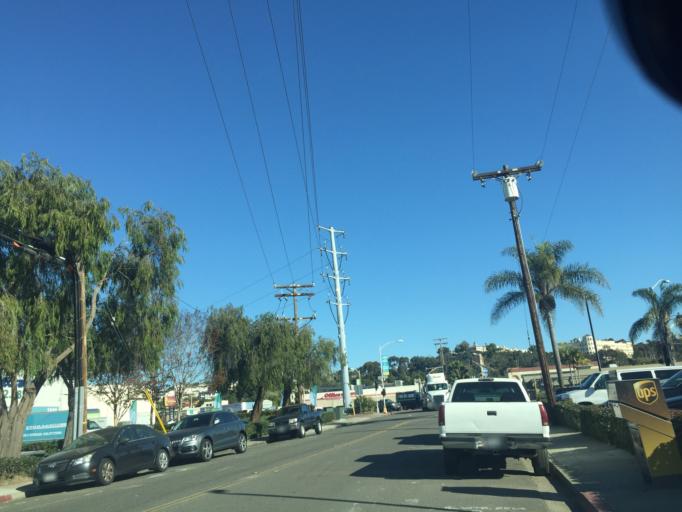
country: US
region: California
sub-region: San Diego County
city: San Diego
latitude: 32.7652
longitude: -117.1991
